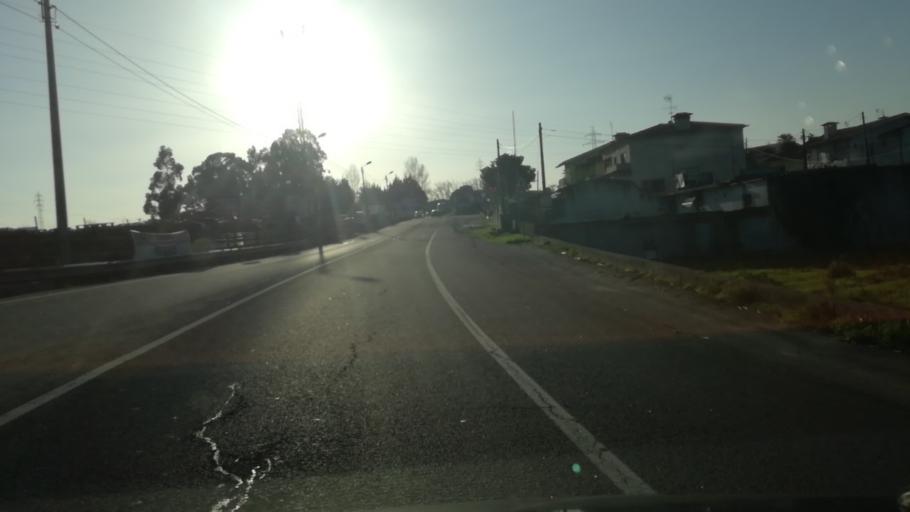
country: PT
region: Braga
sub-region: Vila Nova de Famalicao
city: Ferreiros
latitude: 41.3578
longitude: -8.5497
